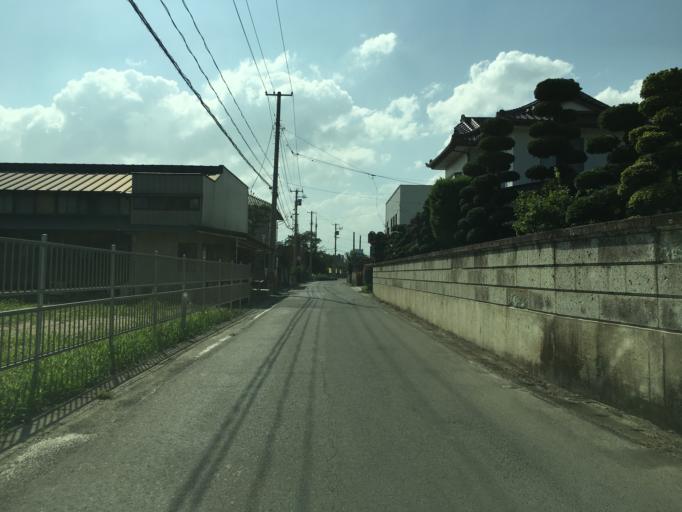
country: JP
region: Miyagi
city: Kakuda
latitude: 37.9431
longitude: 140.8071
